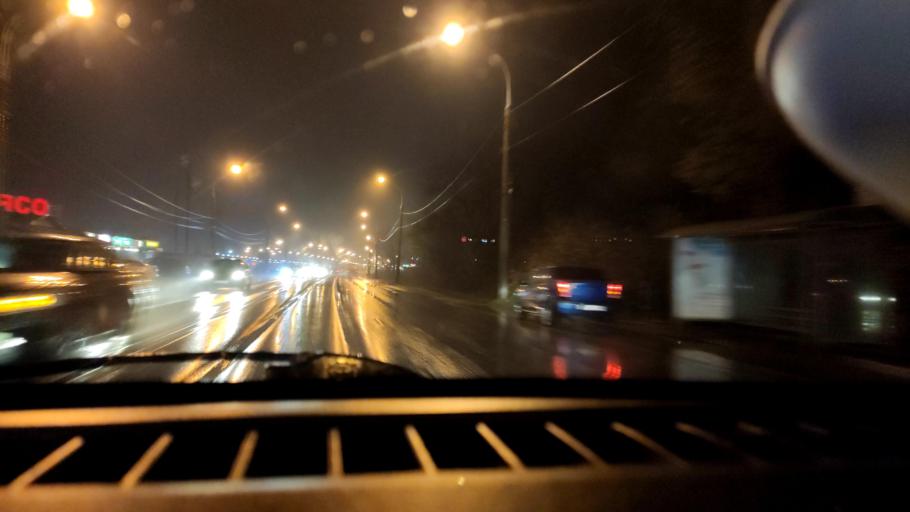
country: RU
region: Samara
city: Samara
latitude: 53.1315
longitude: 50.1731
